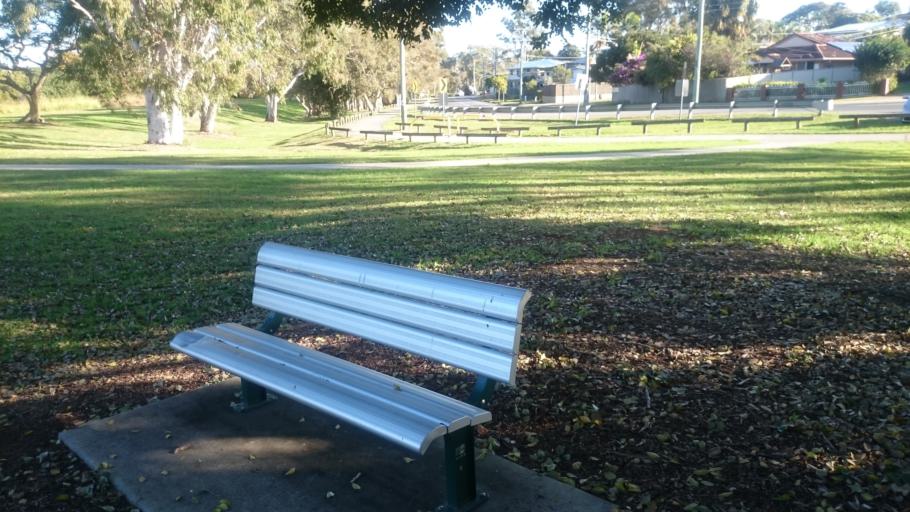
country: AU
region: Queensland
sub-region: Brisbane
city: Manly West
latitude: -27.4719
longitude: 153.1847
